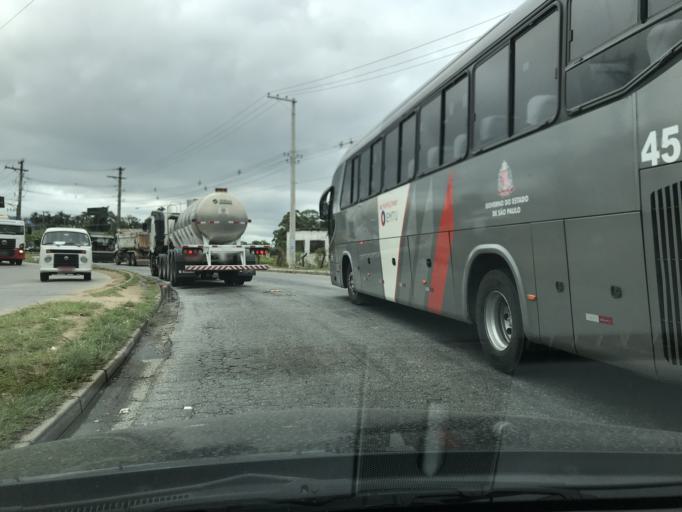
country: BR
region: Sao Paulo
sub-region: Itaquaquecetuba
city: Itaquaquecetuba
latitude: -23.4657
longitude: -46.3356
